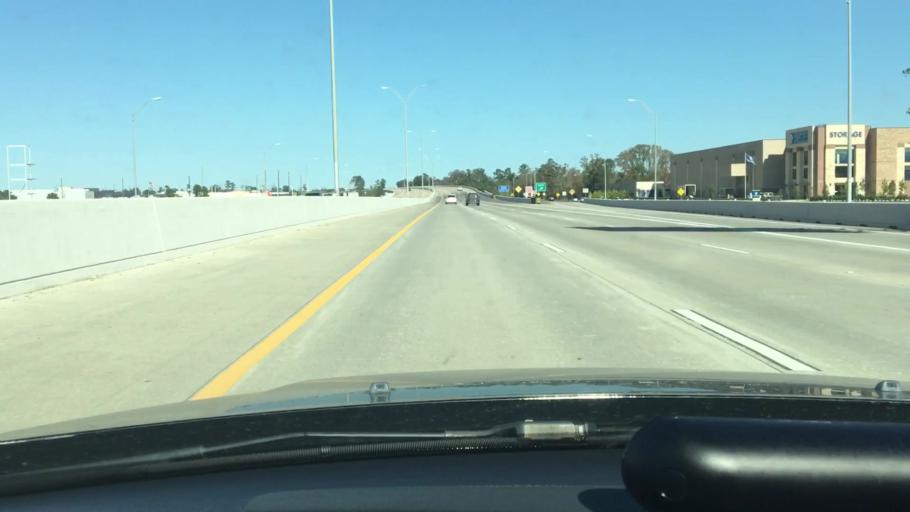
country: US
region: Texas
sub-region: Harris County
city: Atascocita
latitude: 29.9189
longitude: -95.2004
